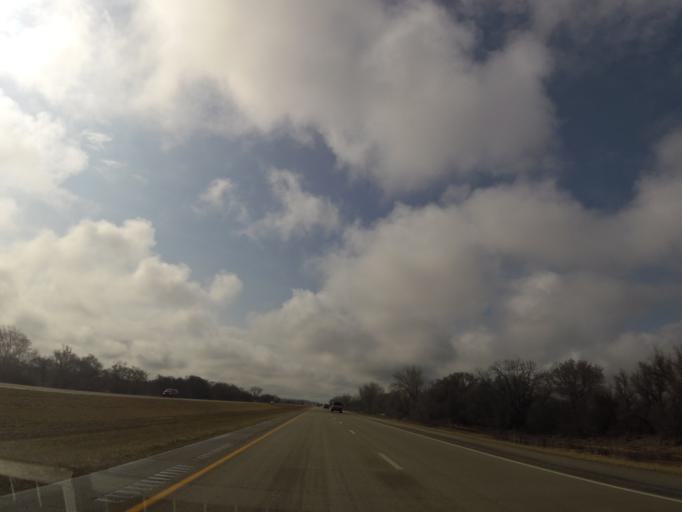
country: US
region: North Dakota
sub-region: Traill County
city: Hillsboro
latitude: 47.6215
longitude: -97.0806
